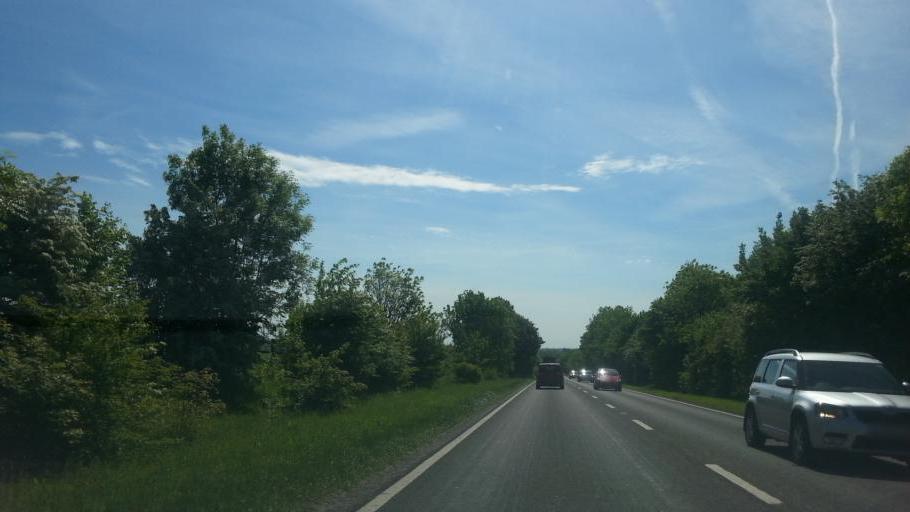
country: GB
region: England
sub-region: Cambridgeshire
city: Huntingdon
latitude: 52.3466
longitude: -0.1616
